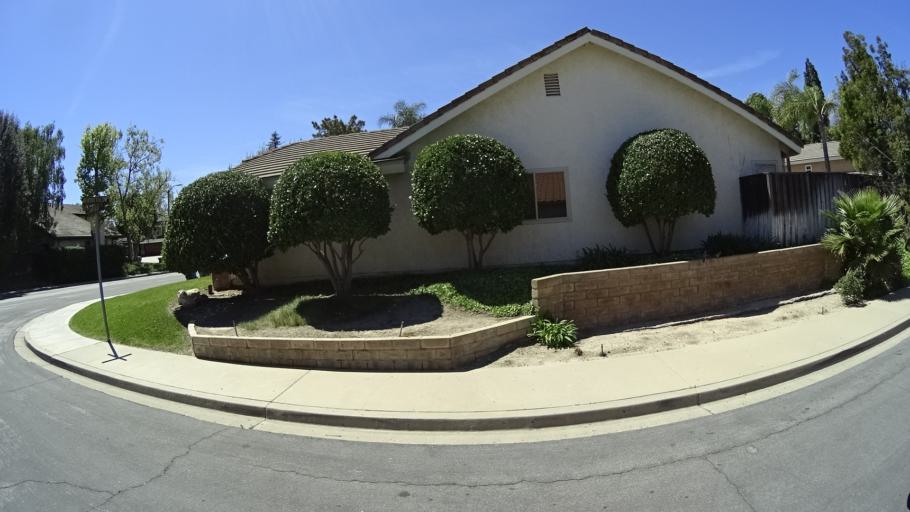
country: US
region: California
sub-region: Ventura County
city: Moorpark
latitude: 34.2232
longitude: -118.8747
